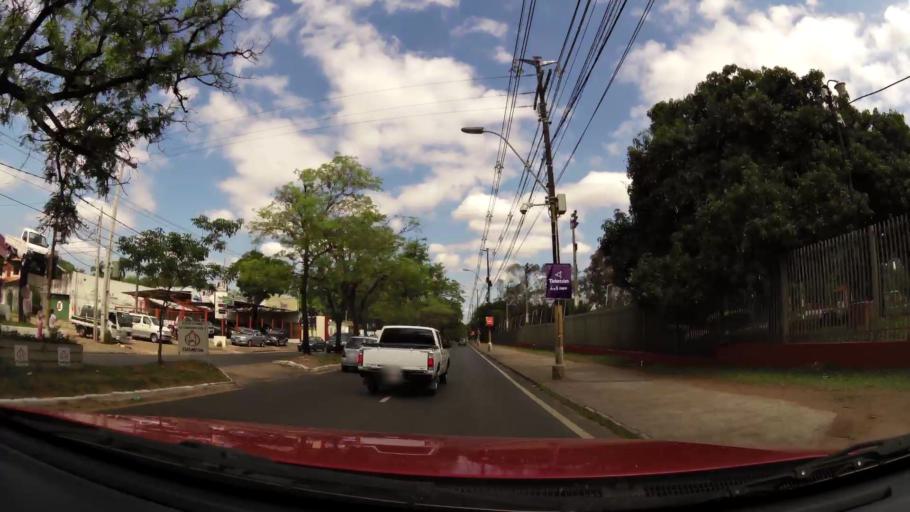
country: PY
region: Central
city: Fernando de la Mora
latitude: -25.3316
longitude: -57.5155
